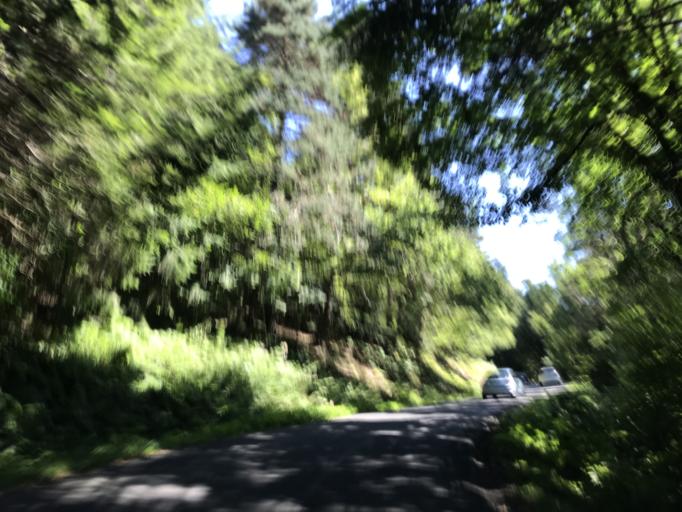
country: FR
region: Auvergne
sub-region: Departement du Puy-de-Dome
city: Job
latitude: 45.6673
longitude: 3.7248
